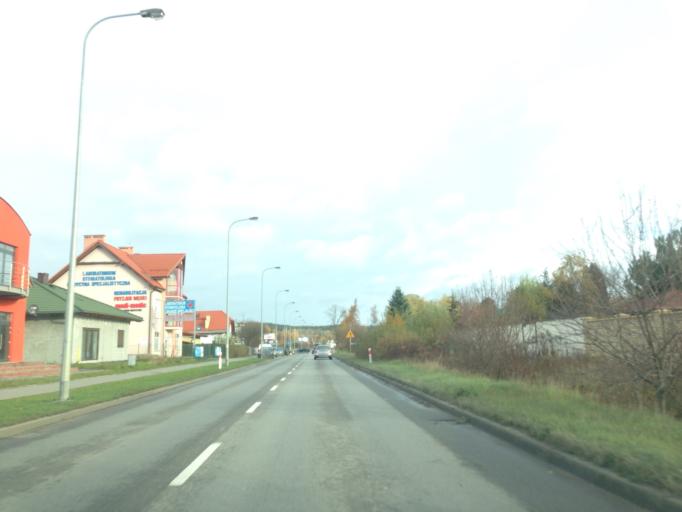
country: PL
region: Pomeranian Voivodeship
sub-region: Powiat gdanski
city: Kolbudy
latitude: 54.2738
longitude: 18.4755
